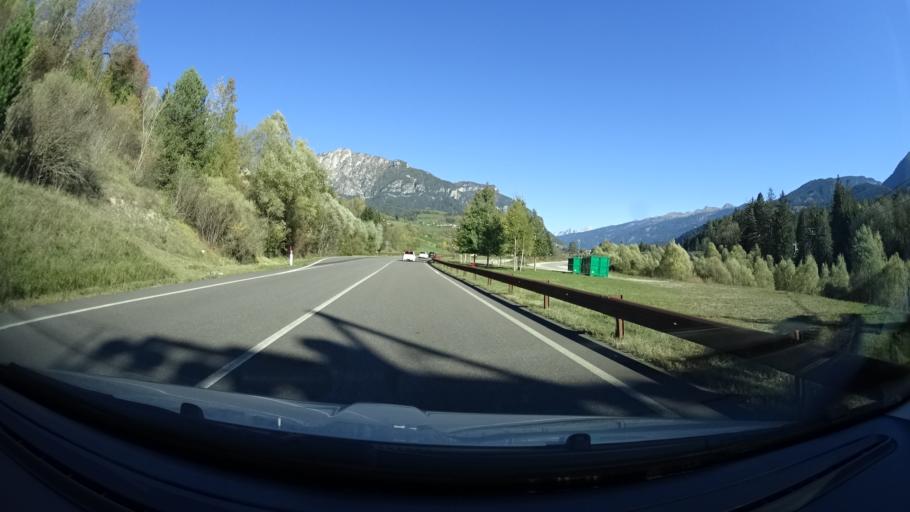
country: IT
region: Trentino-Alto Adige
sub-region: Provincia di Trento
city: Cavalese
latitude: 46.2842
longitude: 11.4671
